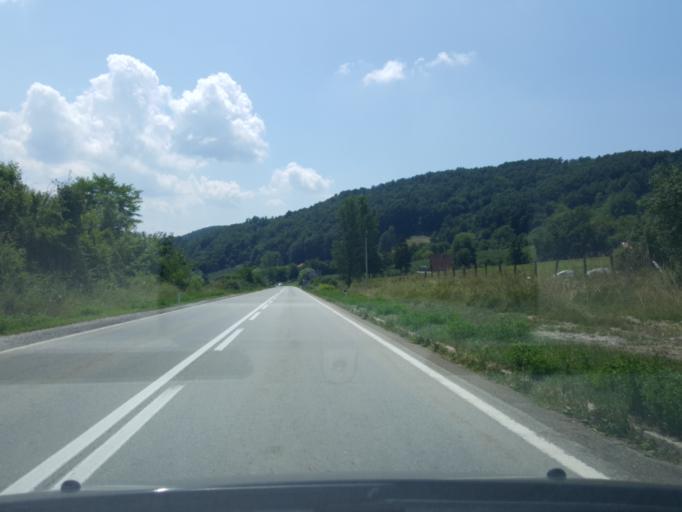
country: RS
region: Central Serbia
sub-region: Moravicki Okrug
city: Gornji Milanovac
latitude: 44.0882
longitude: 20.4792
